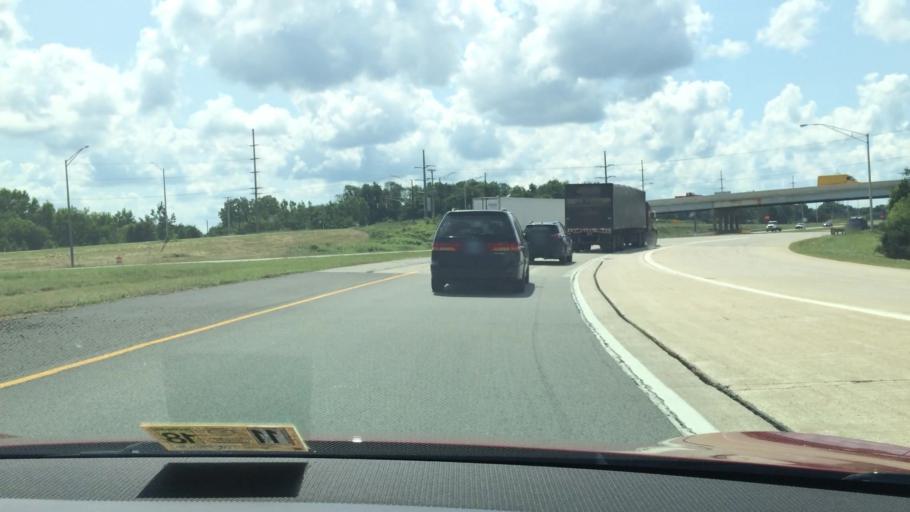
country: US
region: Indiana
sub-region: Saint Joseph County
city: South Bend
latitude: 41.7241
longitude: -86.3400
